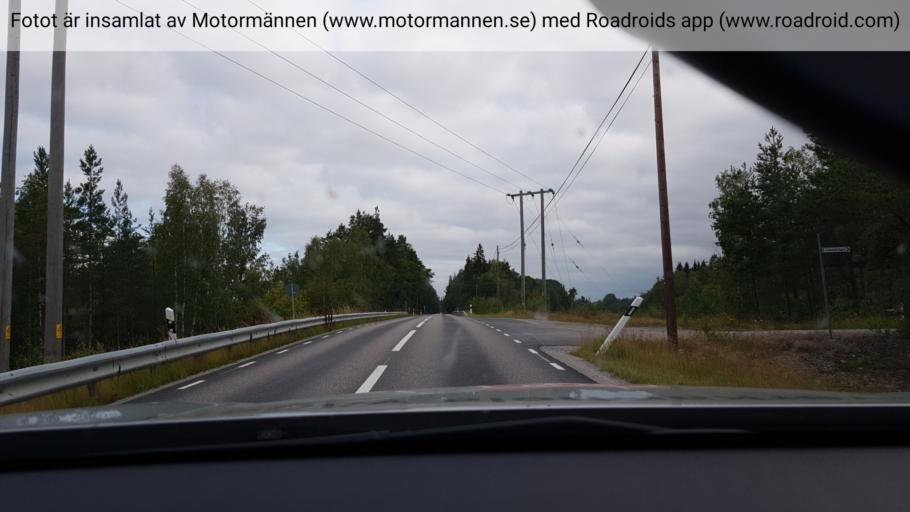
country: SE
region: Stockholm
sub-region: Norrtalje Kommun
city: Rimbo
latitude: 59.8158
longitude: 18.4405
